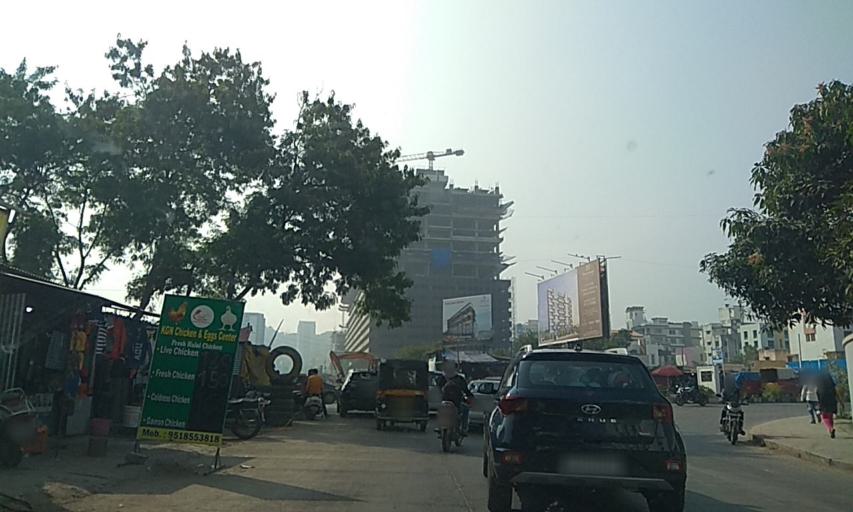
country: IN
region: Maharashtra
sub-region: Pune Division
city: Pimpri
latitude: 18.5589
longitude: 73.7765
